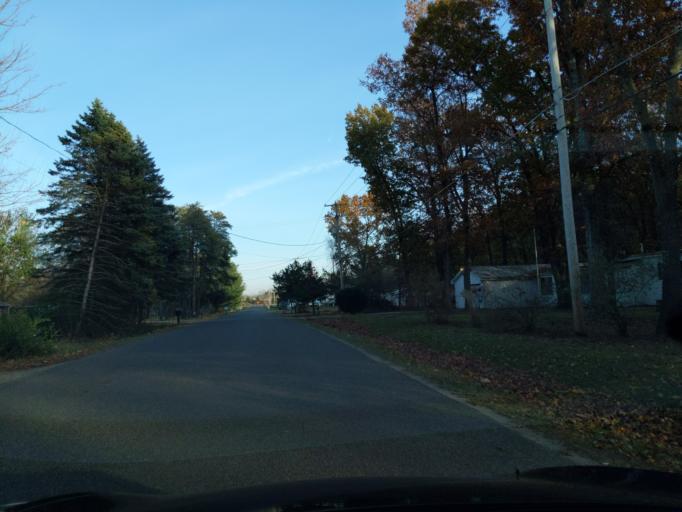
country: US
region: Michigan
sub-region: Clinton County
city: Bath
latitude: 42.7956
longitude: -84.4538
